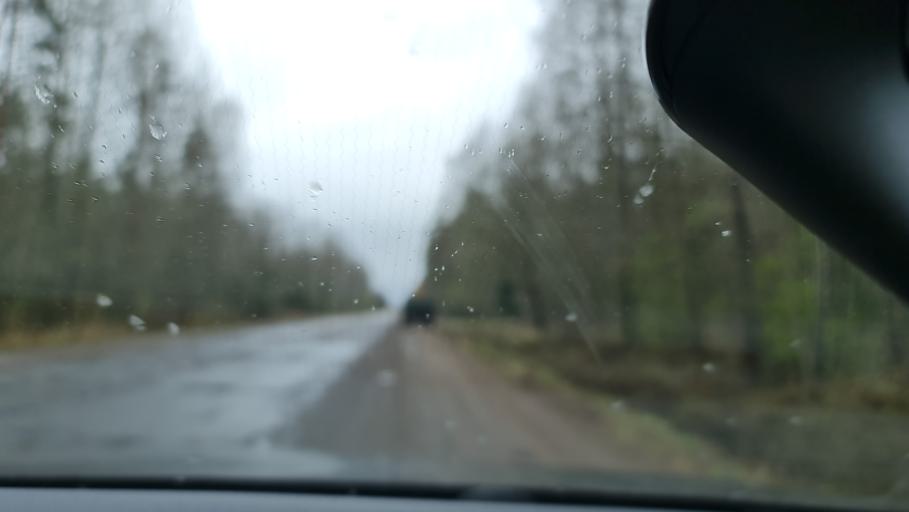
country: RU
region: Novgorod
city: Demyansk
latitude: 57.6729
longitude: 32.5472
